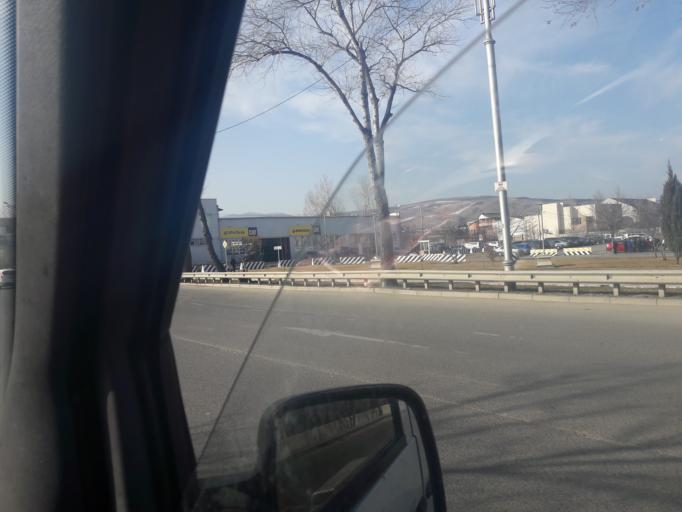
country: GE
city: Zahesi
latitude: 41.7875
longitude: 44.7751
